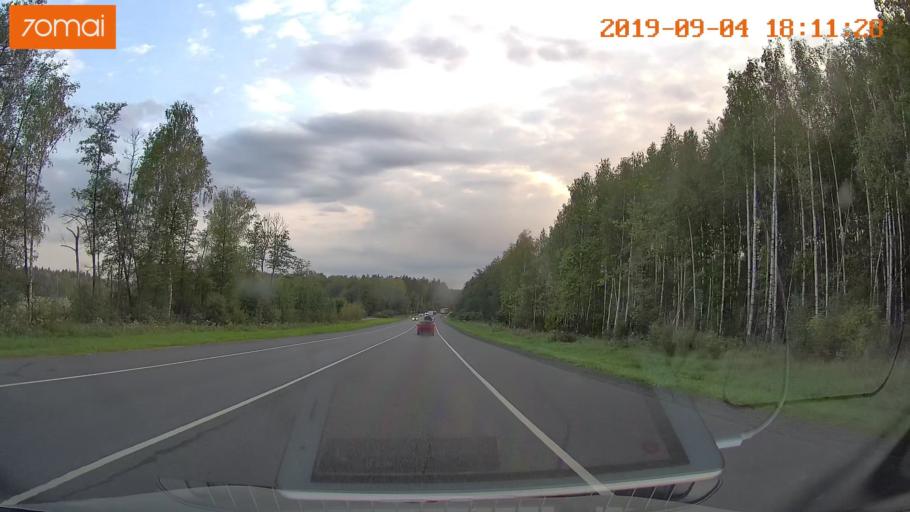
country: RU
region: Moskovskaya
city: Lopatinskiy
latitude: 55.3779
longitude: 38.7543
